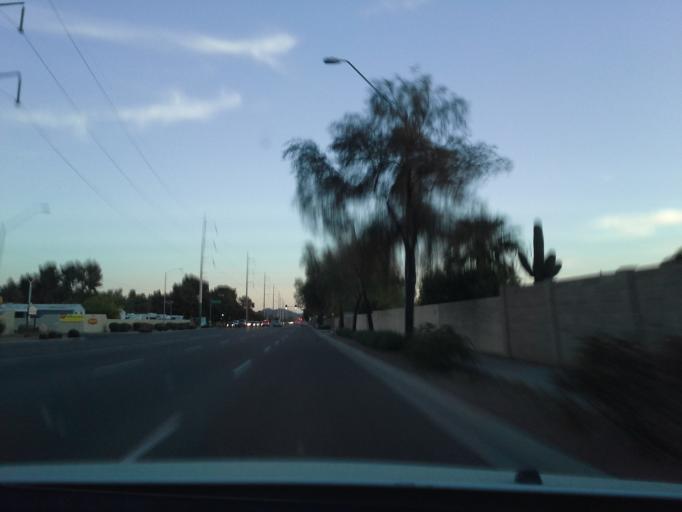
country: US
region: Arizona
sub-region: Maricopa County
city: Glendale
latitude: 33.6494
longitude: -112.0657
